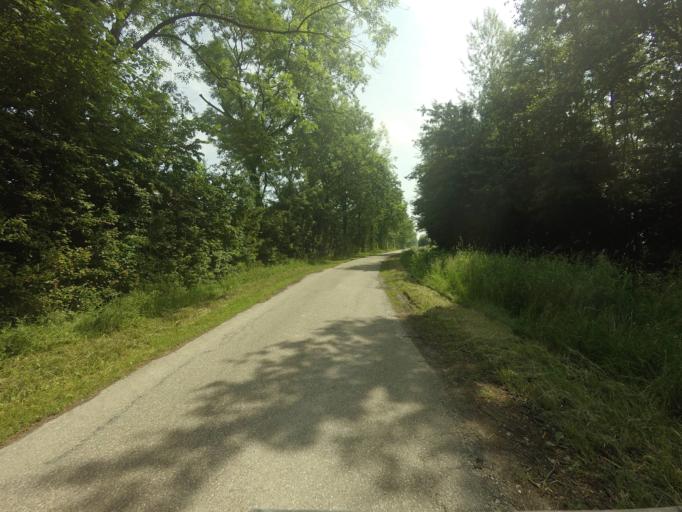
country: NL
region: Gelderland
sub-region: Gemeente Culemborg
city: Culemborg
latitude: 51.9978
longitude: 5.2127
